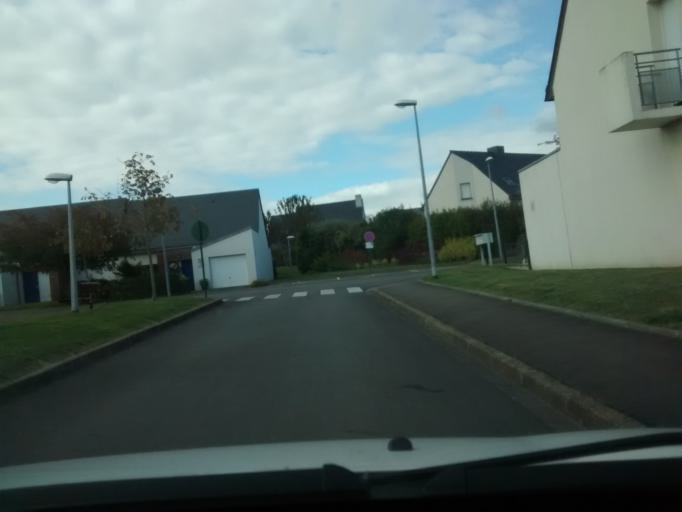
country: FR
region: Brittany
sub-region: Departement d'Ille-et-Vilaine
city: Cesson-Sevigne
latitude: 48.1068
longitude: -1.6058
